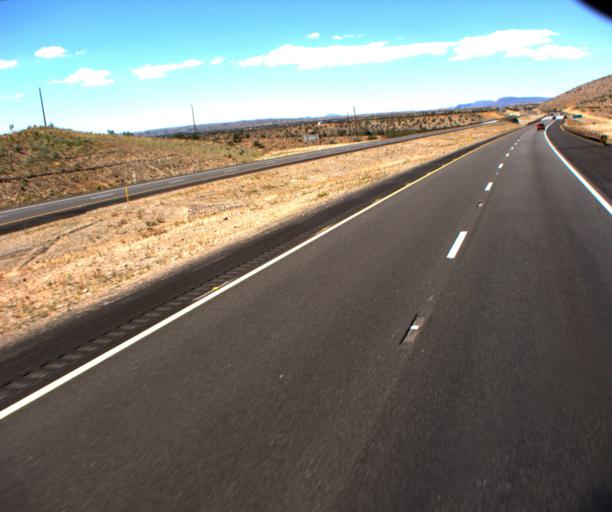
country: US
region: Arizona
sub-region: Mohave County
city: Kingman
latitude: 35.0060
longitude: -113.6644
